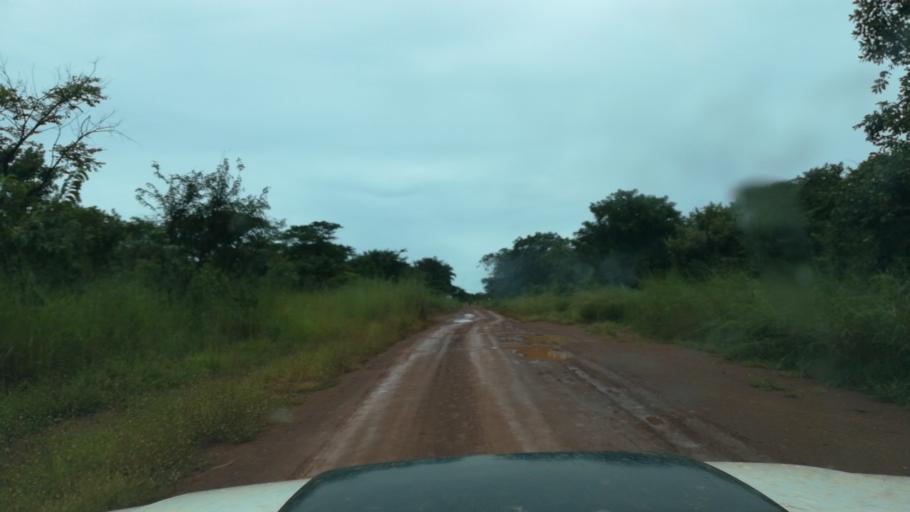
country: ZM
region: Luapula
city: Mwense
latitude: -10.1843
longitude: 28.1215
